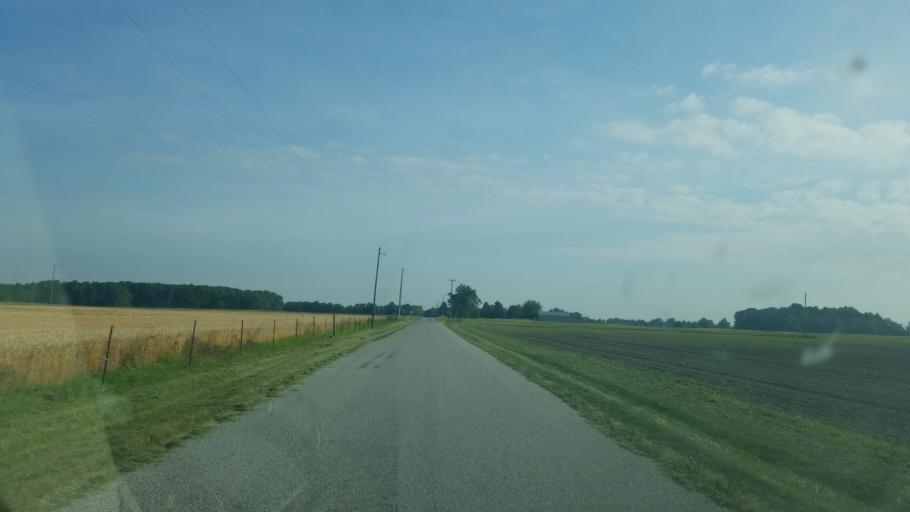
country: US
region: Ohio
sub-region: Hancock County
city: Arlington
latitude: 40.8109
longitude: -83.6705
